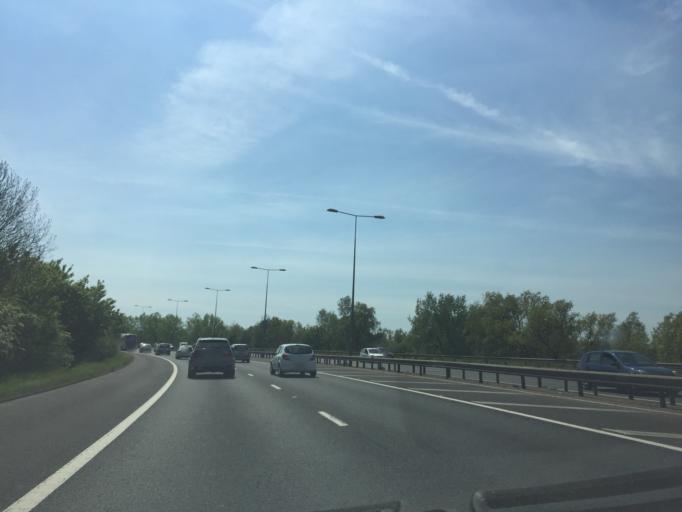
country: GB
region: England
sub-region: Essex
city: Buckhurst Hill
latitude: 51.6096
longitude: 0.0487
